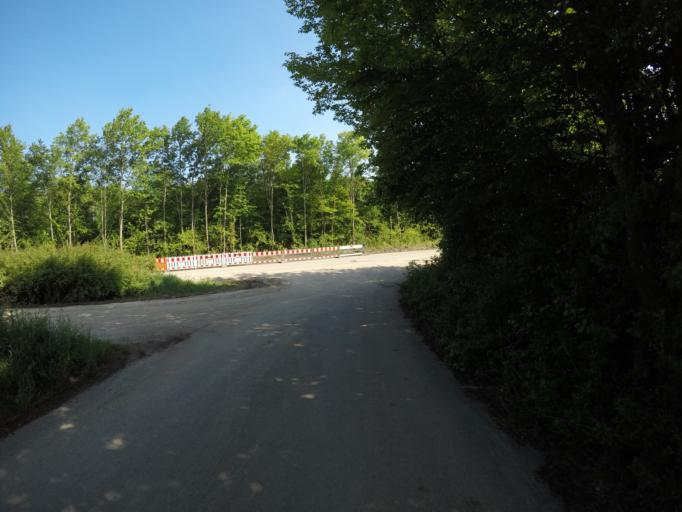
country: DE
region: Baden-Wuerttemberg
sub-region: Tuebingen Region
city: Reutlingen
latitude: 48.4775
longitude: 9.1831
